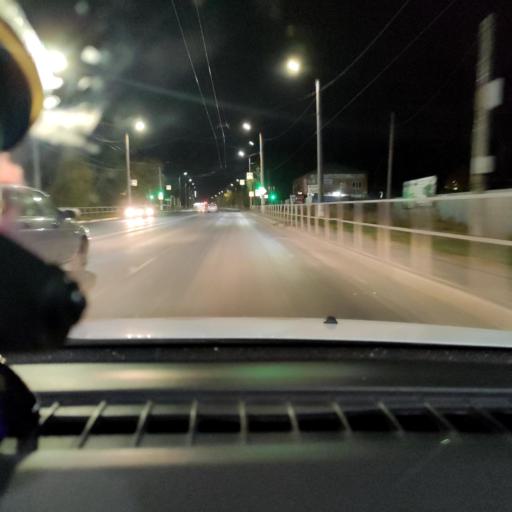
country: RU
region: Samara
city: Novokuybyshevsk
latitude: 53.0953
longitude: 49.9402
